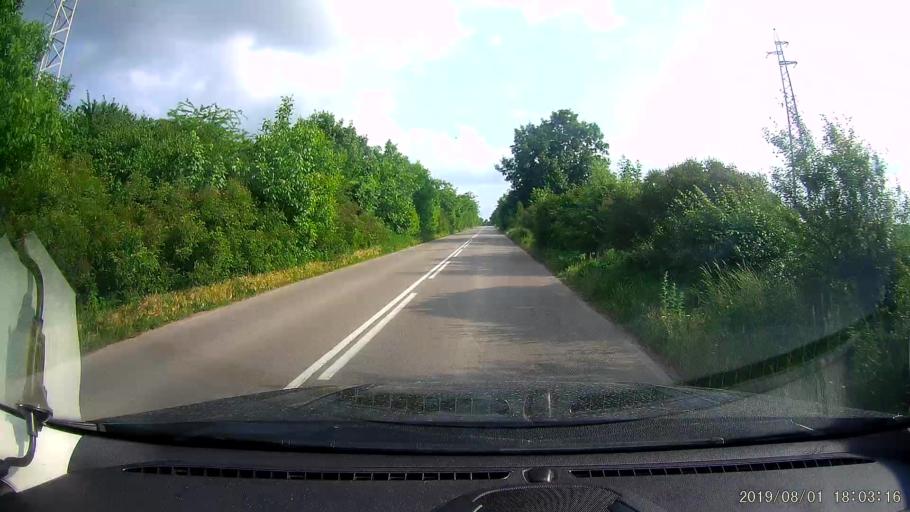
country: BG
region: Silistra
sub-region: Obshtina Alfatar
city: Alfatar
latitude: 43.9315
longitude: 27.2900
